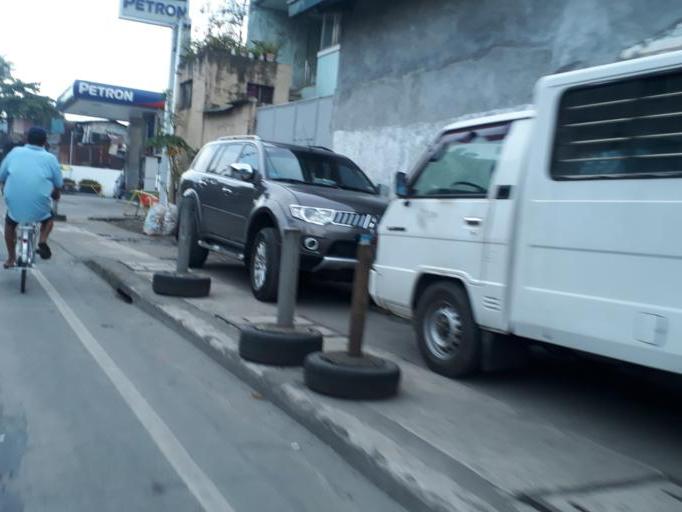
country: PH
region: Calabarzon
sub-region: Province of Rizal
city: Valenzuela
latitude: 14.6955
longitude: 120.9541
